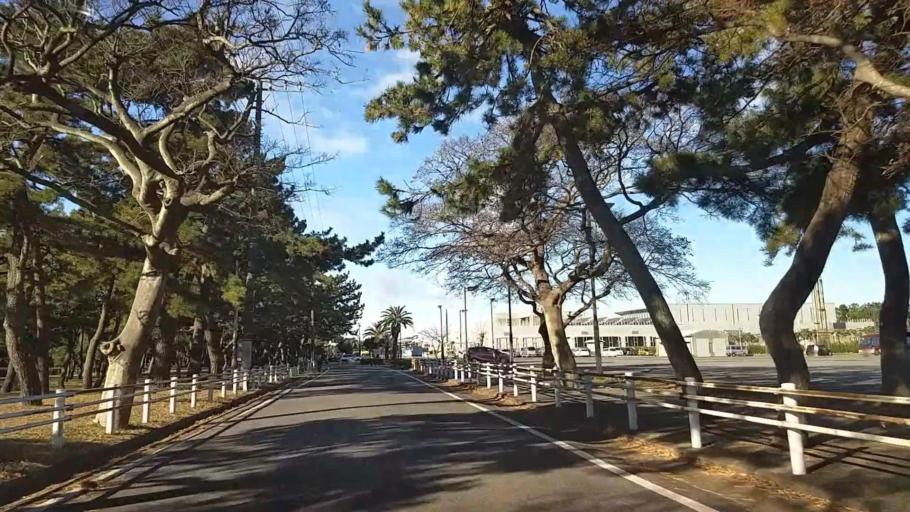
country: JP
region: Chiba
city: Futtsu
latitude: 35.3129
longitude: 139.8053
